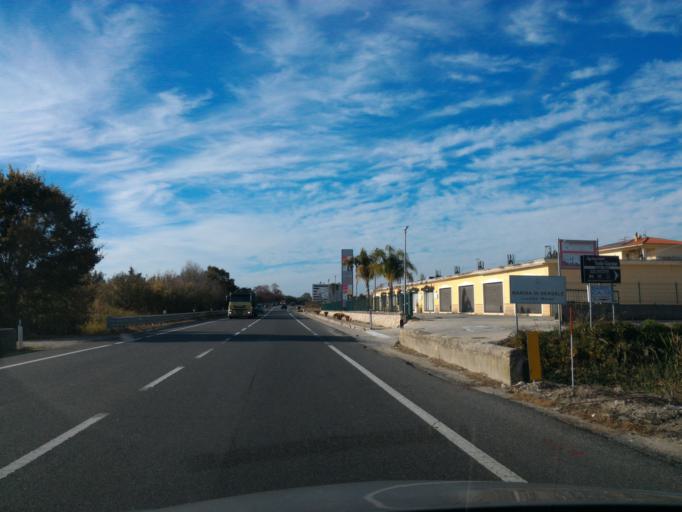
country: IT
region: Calabria
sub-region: Provincia di Catanzaro
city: Cropani Marina
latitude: 38.9148
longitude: 16.7843
